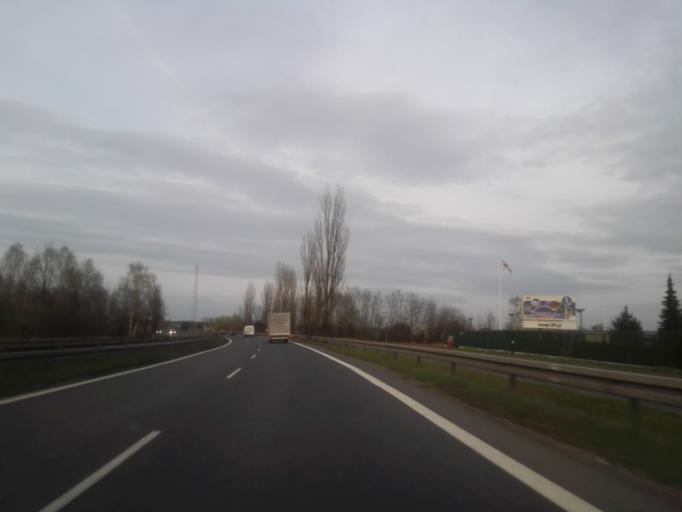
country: PL
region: Masovian Voivodeship
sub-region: Powiat pruszkowski
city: Nadarzyn
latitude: 52.0845
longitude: 20.8035
